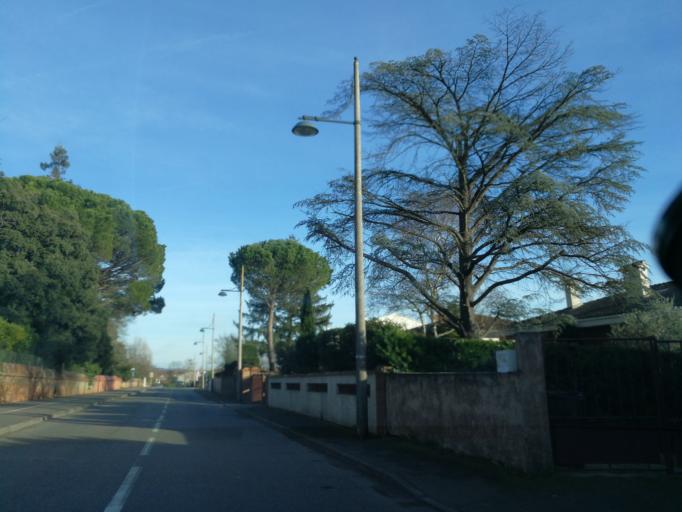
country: FR
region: Midi-Pyrenees
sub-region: Departement de la Haute-Garonne
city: Saint-Jean
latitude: 43.6525
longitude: 1.4946
